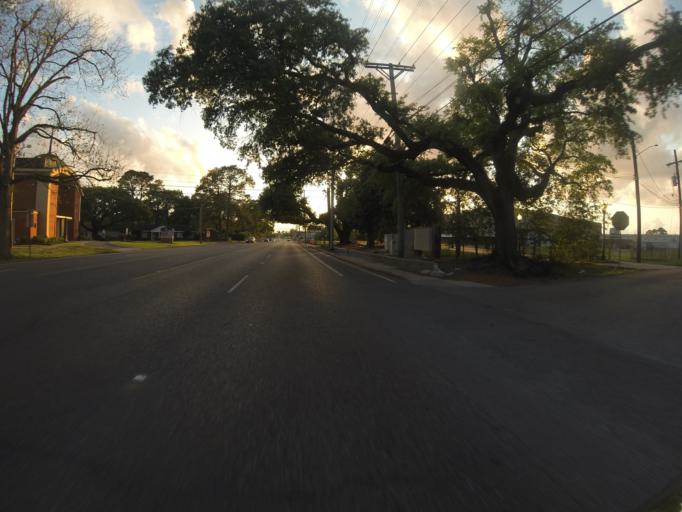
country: US
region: Louisiana
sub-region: Lafayette Parish
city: Lafayette
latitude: 30.2101
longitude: -92.0311
